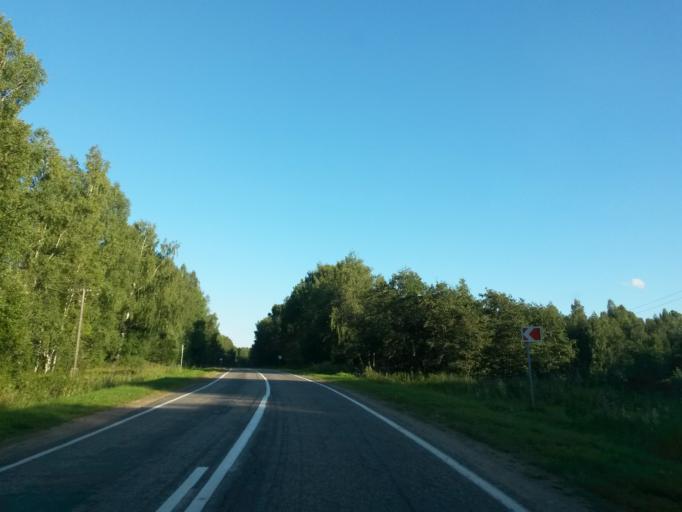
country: RU
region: Jaroslavl
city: Tutayev
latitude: 57.9262
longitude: 39.5063
